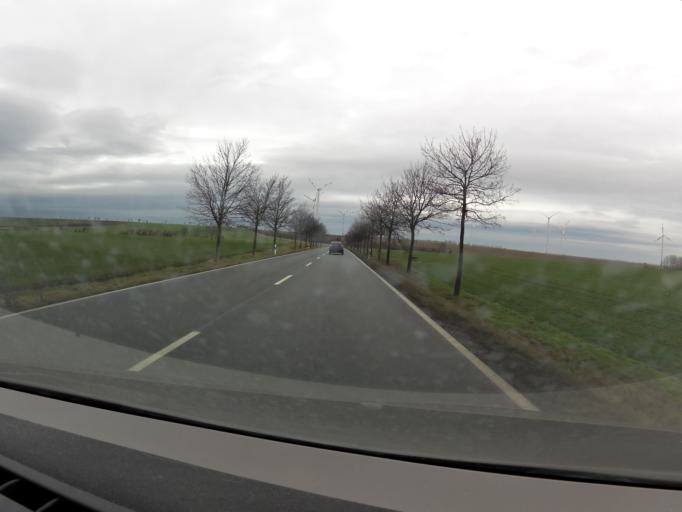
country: DE
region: Saxony-Anhalt
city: Aschersleben
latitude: 51.7009
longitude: 11.4572
